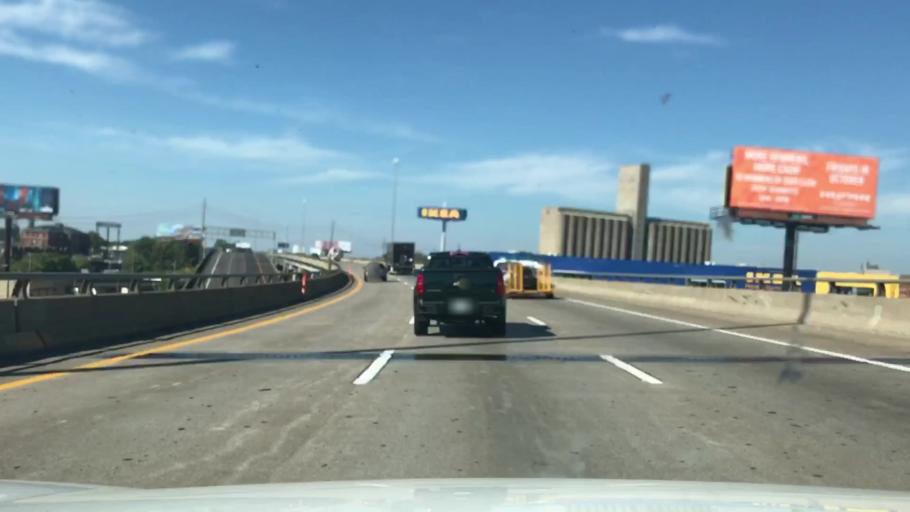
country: US
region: Missouri
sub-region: City of Saint Louis
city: St. Louis
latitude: 38.6324
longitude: -90.2411
